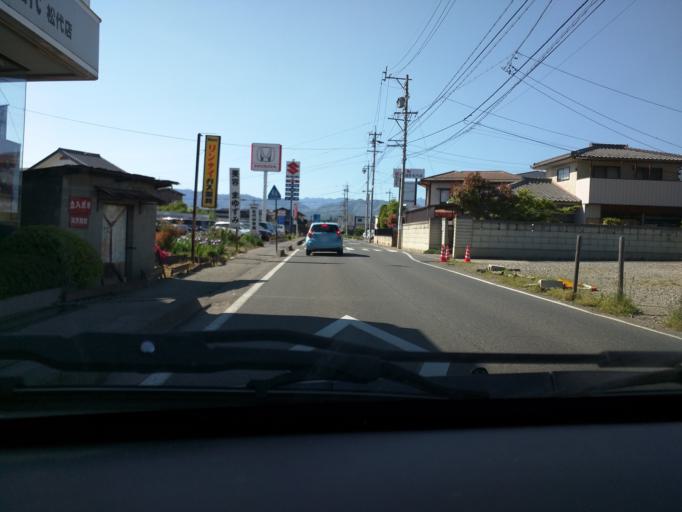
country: JP
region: Nagano
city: Nagano-shi
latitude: 36.5681
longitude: 138.2008
